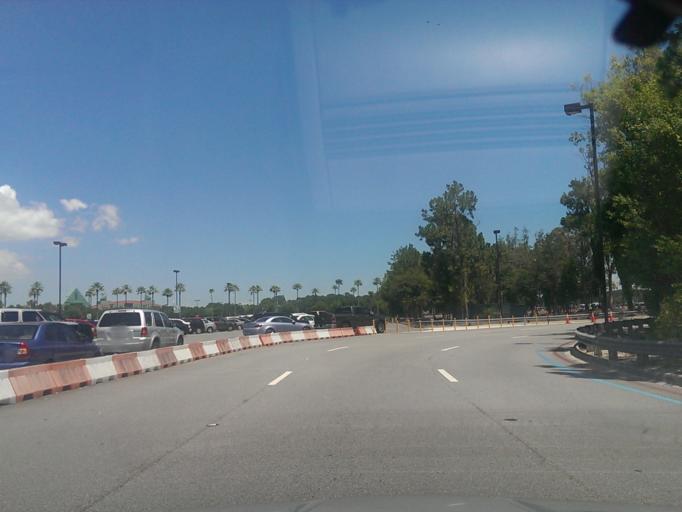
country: US
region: Florida
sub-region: Osceola County
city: Celebration
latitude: 28.3560
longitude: -81.5547
